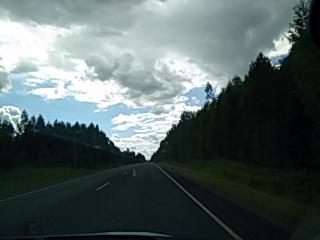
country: FI
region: Haeme
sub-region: Haemeenlinna
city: Renko
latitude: 60.8683
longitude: 24.2024
